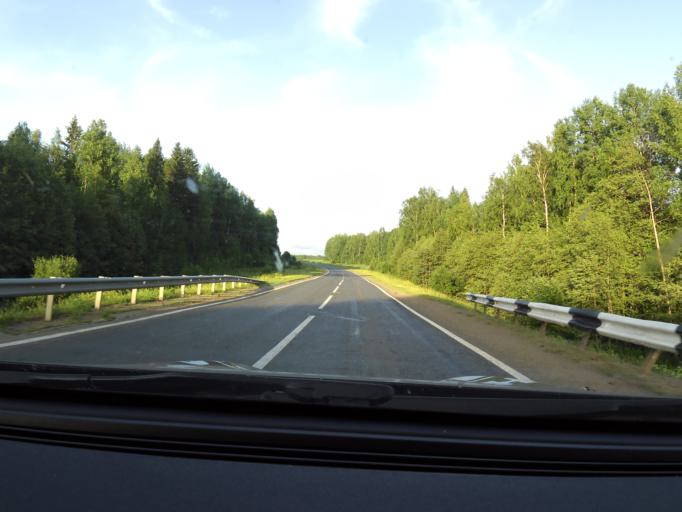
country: RU
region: Perm
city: Siva
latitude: 58.4858
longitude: 54.1405
